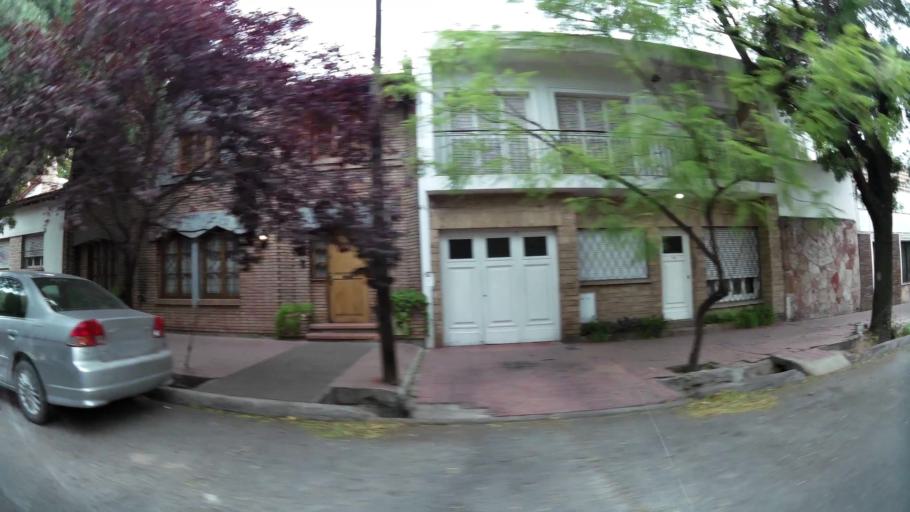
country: AR
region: Mendoza
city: Mendoza
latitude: -32.8833
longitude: -68.8519
